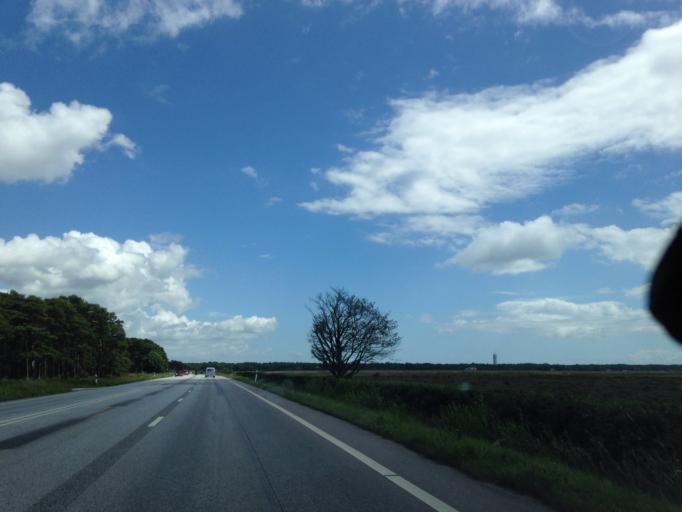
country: SE
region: Skane
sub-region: Vellinge Kommun
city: Skanor med Falsterbo
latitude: 55.4050
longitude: 12.8868
